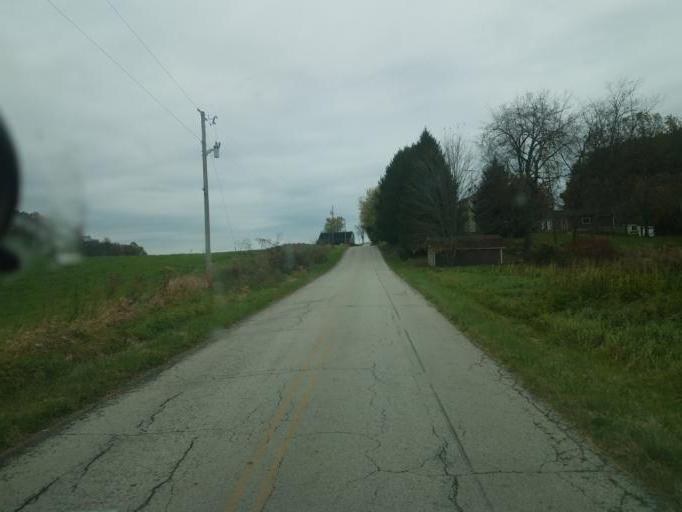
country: US
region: Ohio
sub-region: Ashland County
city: Loudonville
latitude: 40.6304
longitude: -82.1684
